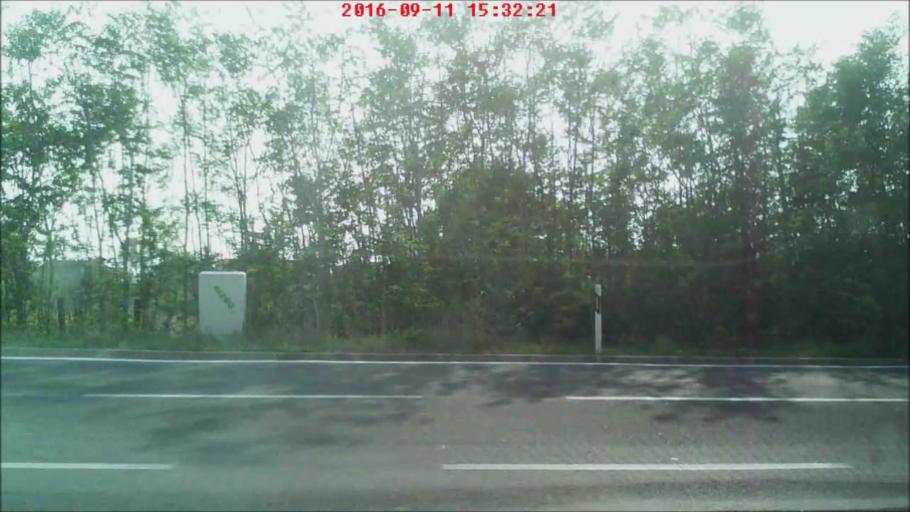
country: HR
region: Zadarska
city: Nin
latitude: 44.2533
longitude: 15.1588
